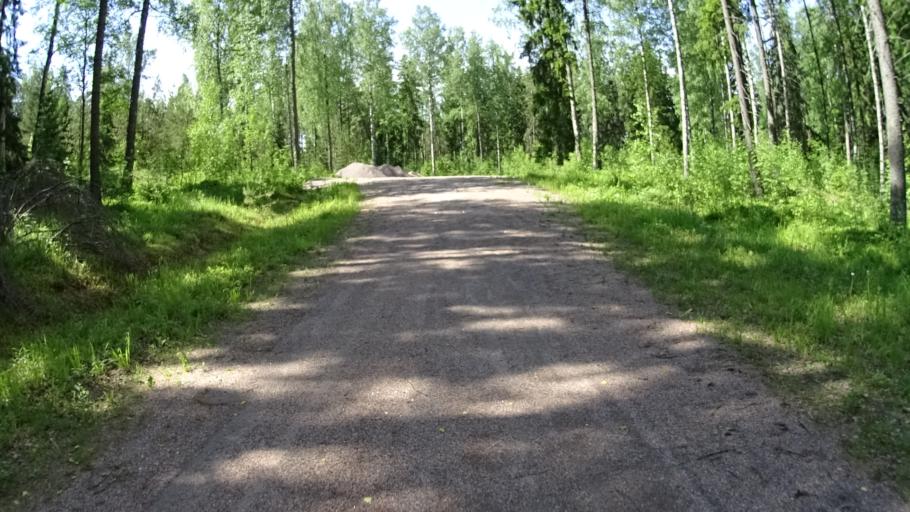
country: FI
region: Uusimaa
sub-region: Helsinki
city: Kilo
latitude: 60.3122
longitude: 24.7940
